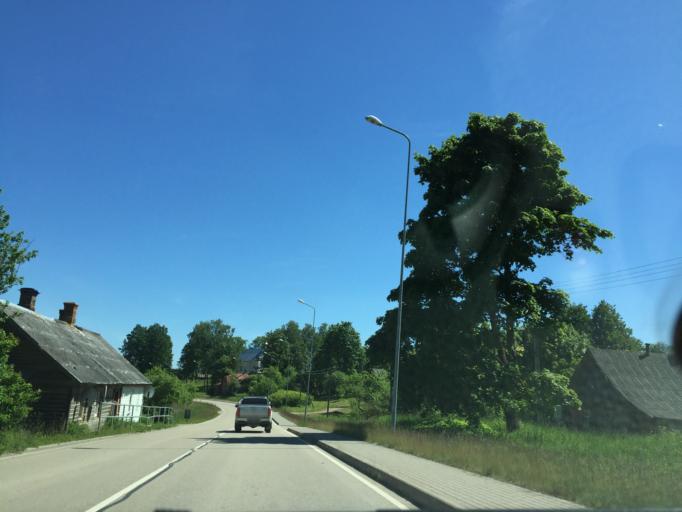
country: LV
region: Preilu Rajons
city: Jaunaglona
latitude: 56.2359
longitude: 27.2274
